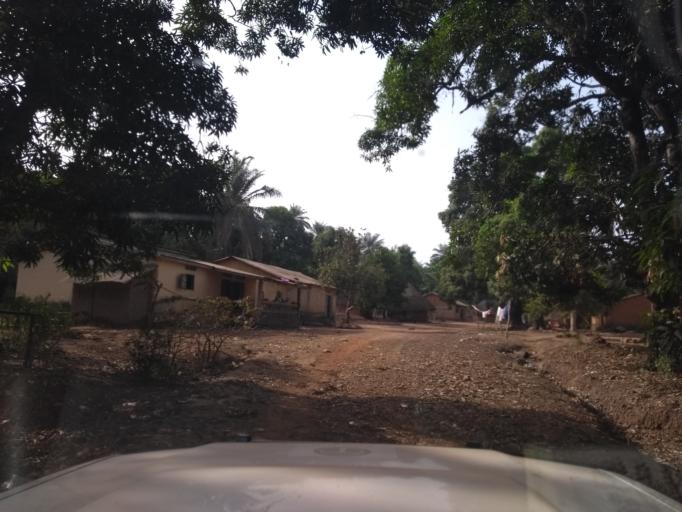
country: GN
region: Kindia
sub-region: Prefecture de Dubreka
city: Dubreka
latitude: 9.8336
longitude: -13.5576
